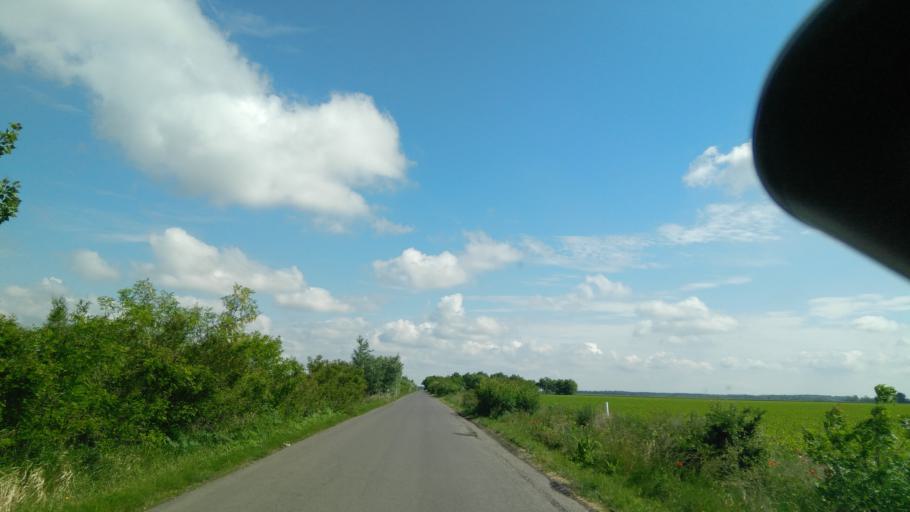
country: HU
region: Bekes
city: Bekes
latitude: 46.8043
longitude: 21.1440
